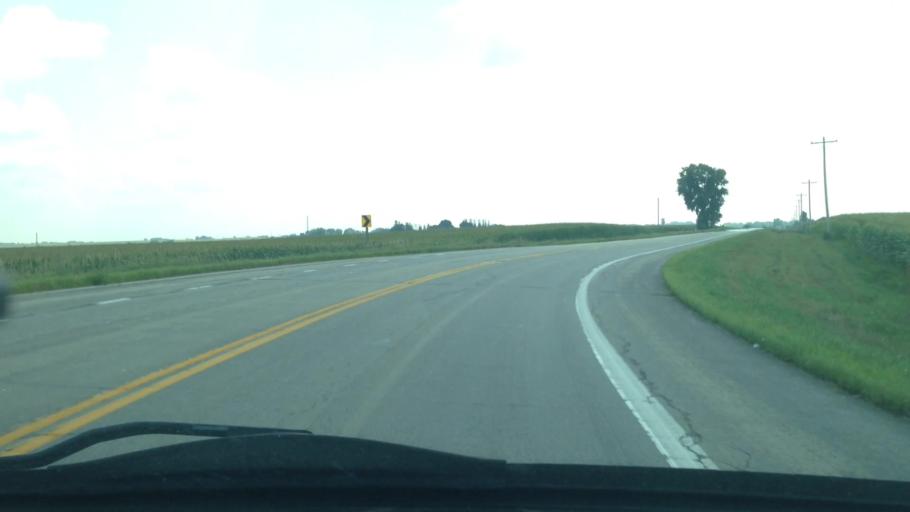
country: US
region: Minnesota
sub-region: Olmsted County
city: Rochester
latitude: 43.9554
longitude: -92.4189
